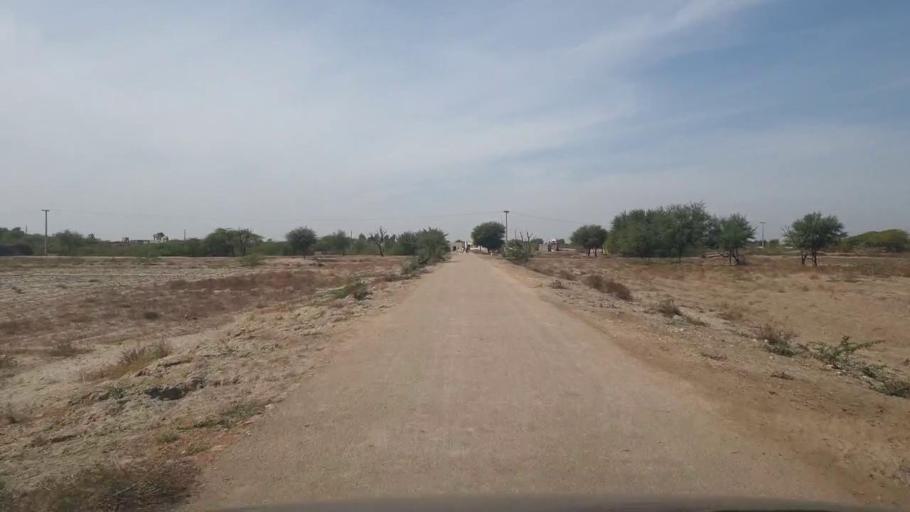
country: PK
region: Sindh
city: Kunri
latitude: 25.3342
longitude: 69.5817
